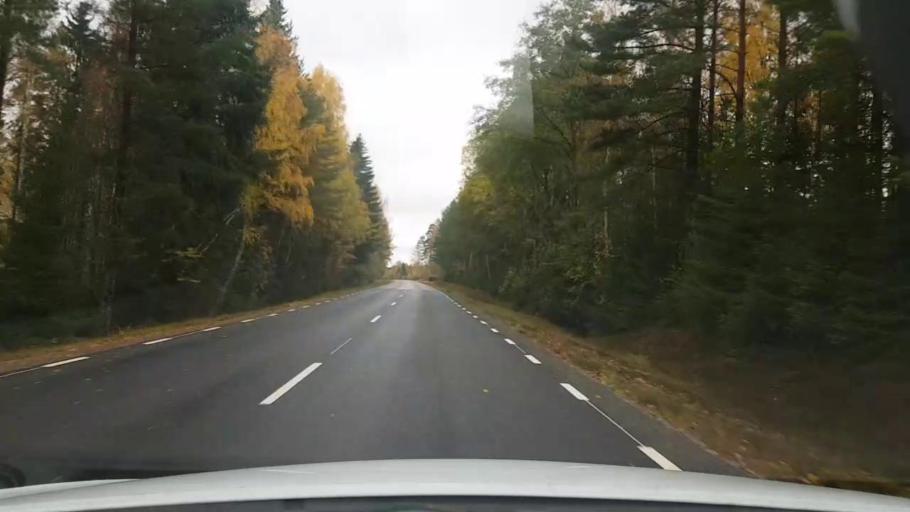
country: SE
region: OErebro
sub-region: Laxa Kommun
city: Laxa
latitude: 58.8524
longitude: 14.5480
